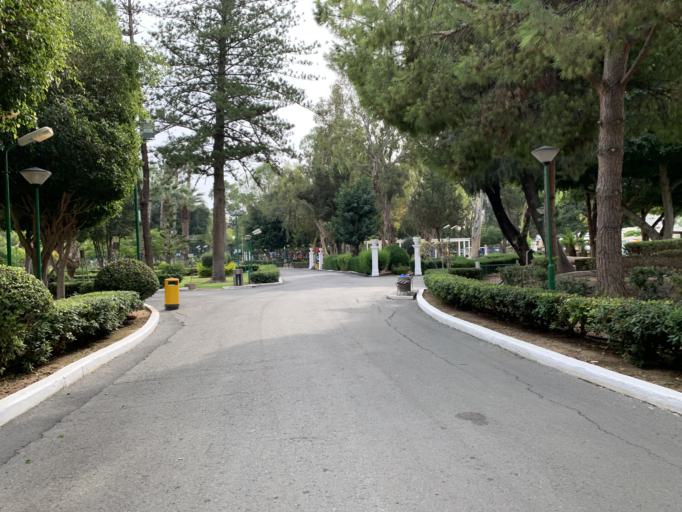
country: CY
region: Limassol
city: Limassol
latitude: 34.6840
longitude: 33.0541
